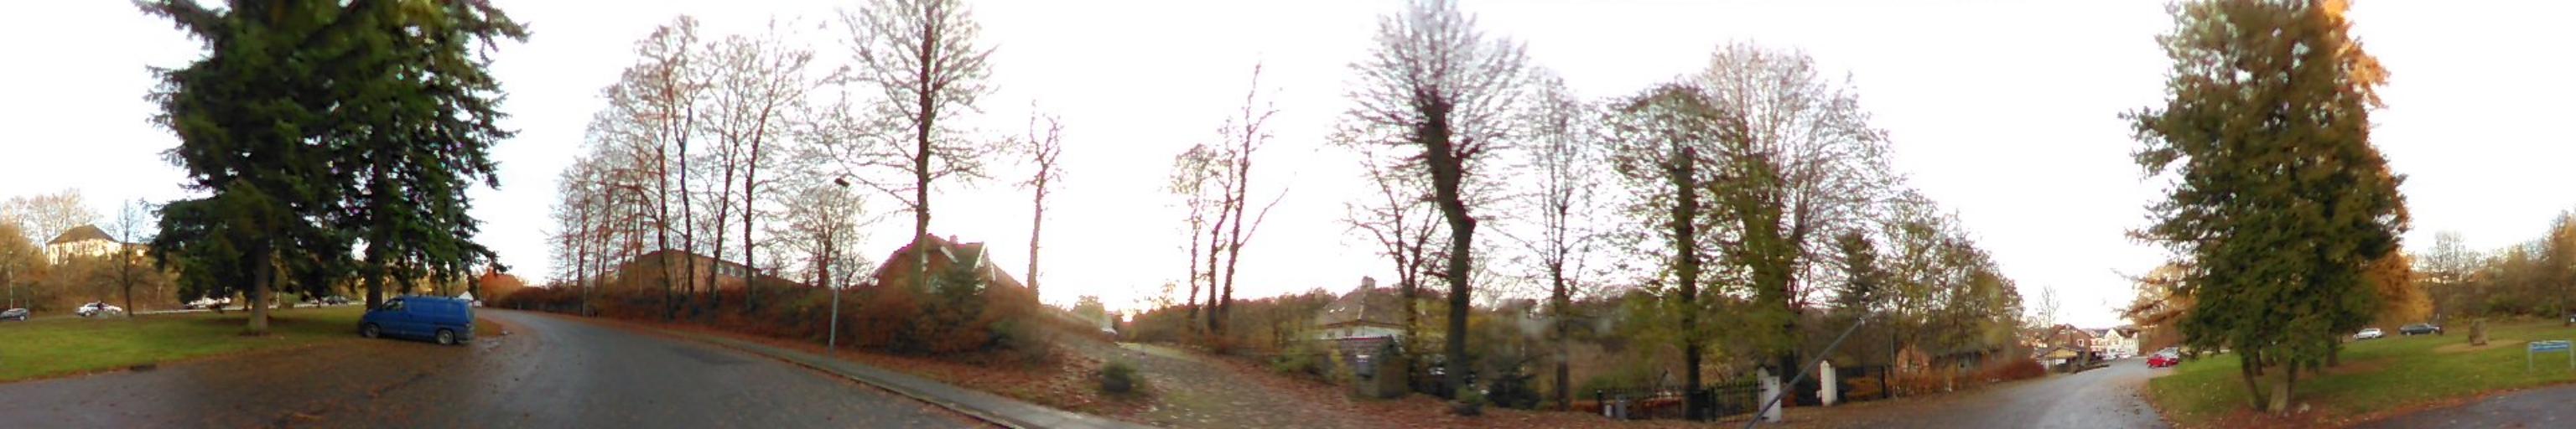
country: DK
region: South Denmark
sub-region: Vejle Kommune
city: Vejle
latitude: 55.6974
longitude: 9.5363
